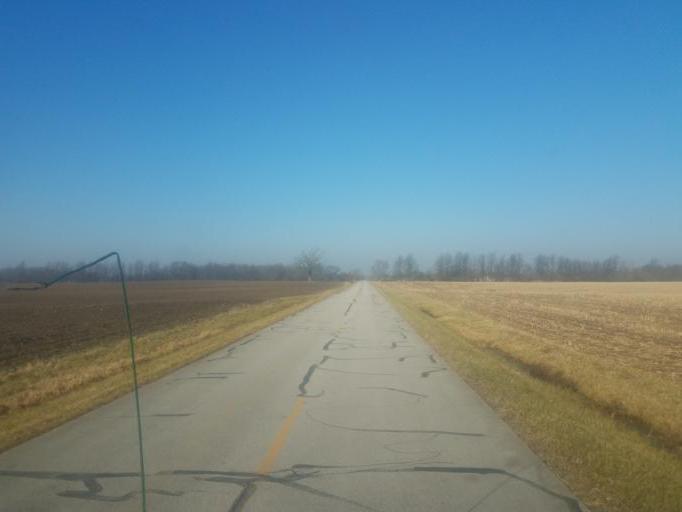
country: US
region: Ohio
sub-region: Seneca County
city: Tiffin
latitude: 41.0383
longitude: -82.9979
